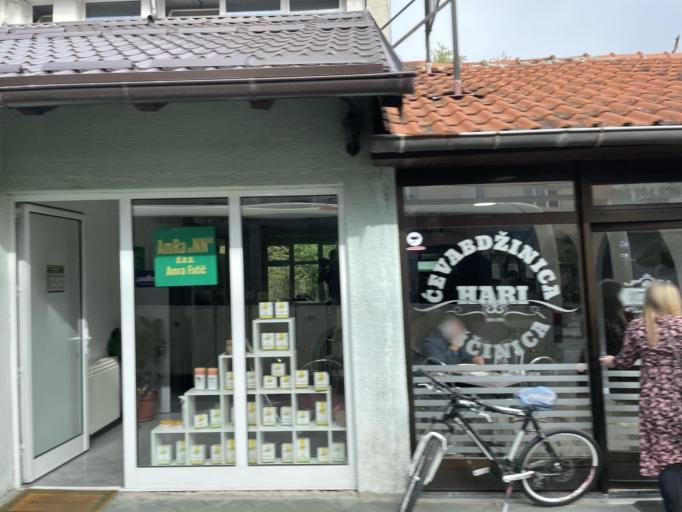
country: BA
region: Federation of Bosnia and Herzegovina
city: Hadzici
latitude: 43.8217
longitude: 18.2011
